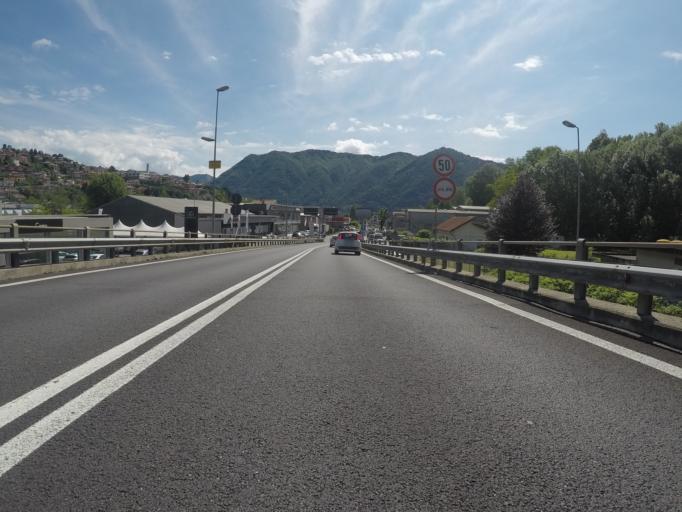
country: IT
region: Lombardy
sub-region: Provincia di Como
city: Maslianico
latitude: 45.8378
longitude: 9.0550
